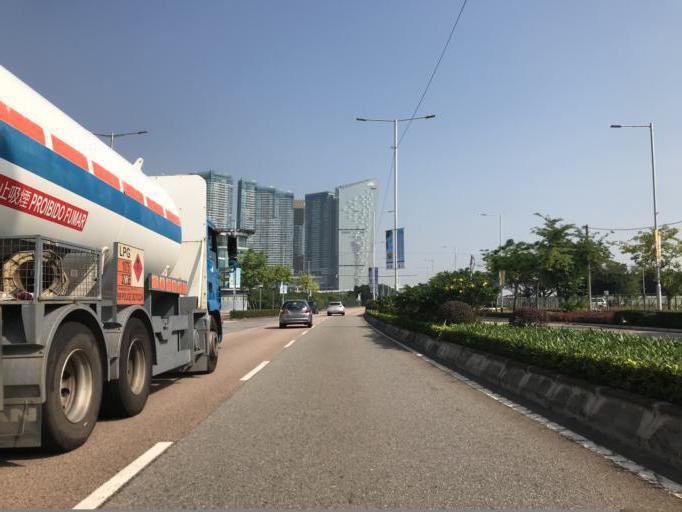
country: MO
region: Macau
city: Macau
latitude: 22.1819
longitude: 113.5403
